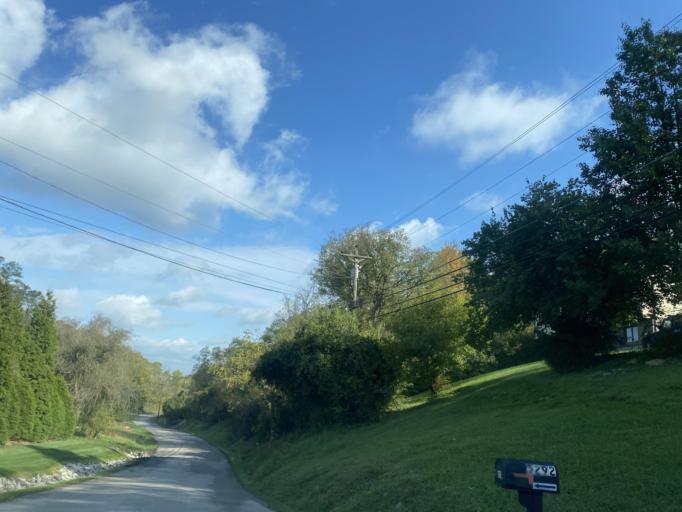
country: US
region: Kentucky
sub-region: Campbell County
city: Cold Spring
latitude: 39.0268
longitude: -84.4192
